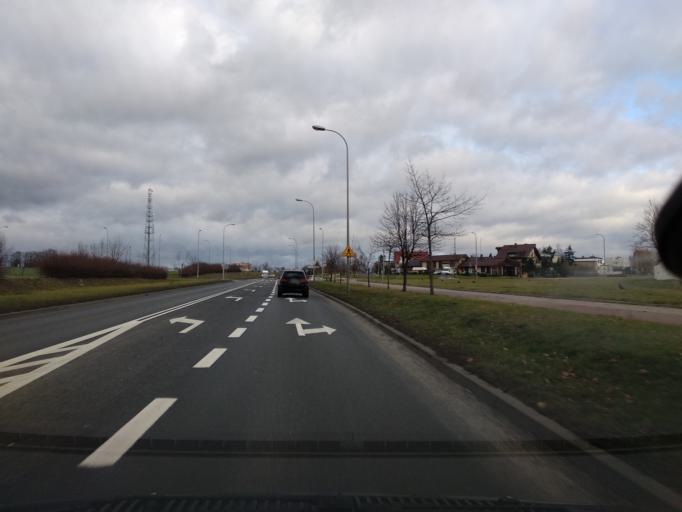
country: PL
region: Greater Poland Voivodeship
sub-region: Kalisz
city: Kalisz
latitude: 51.7774
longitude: 18.0788
